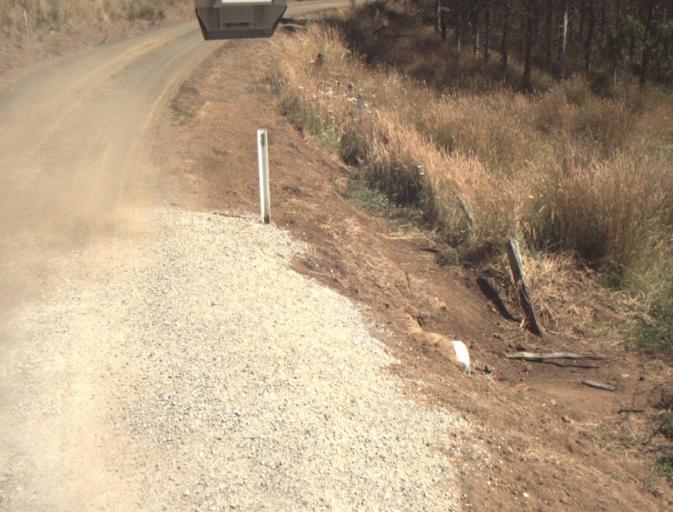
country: AU
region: Tasmania
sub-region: Dorset
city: Scottsdale
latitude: -41.3478
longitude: 147.4536
